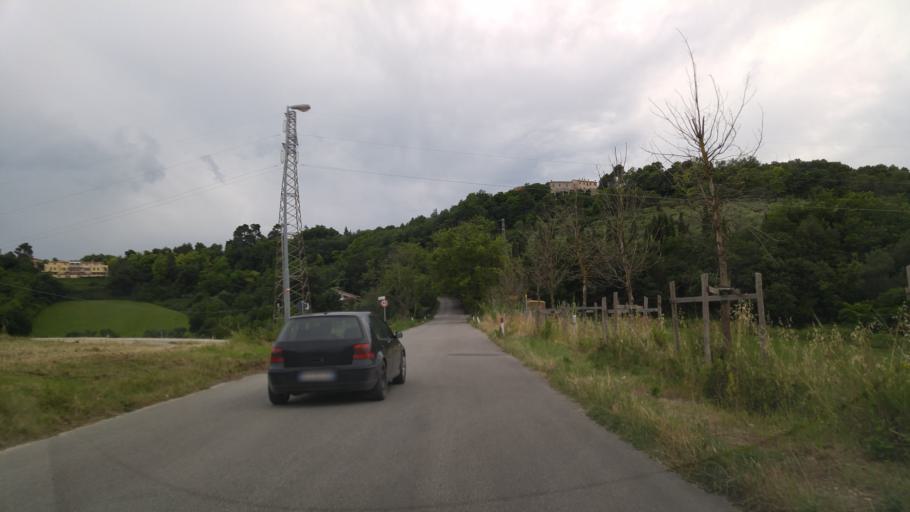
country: IT
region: The Marches
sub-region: Provincia di Pesaro e Urbino
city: Fenile
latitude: 43.8639
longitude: 12.9344
